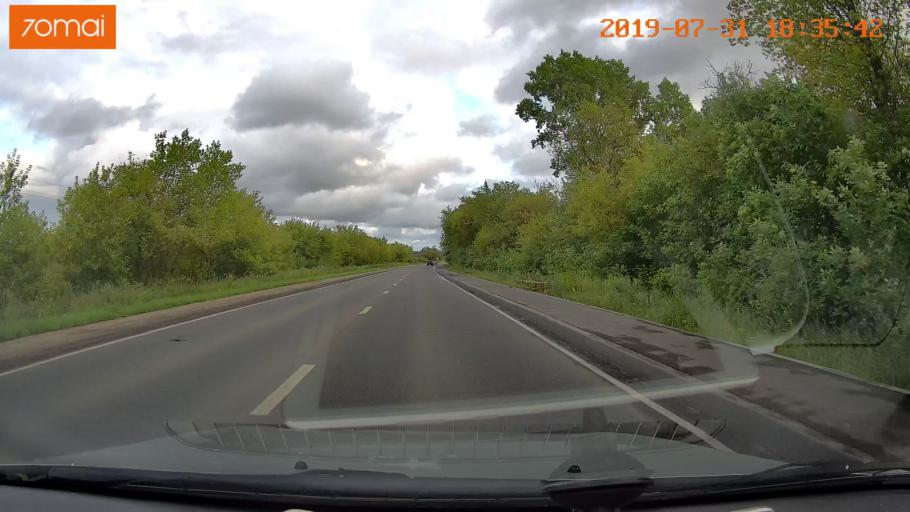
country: RU
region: Moskovskaya
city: Voskresensk
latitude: 55.2933
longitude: 38.6717
